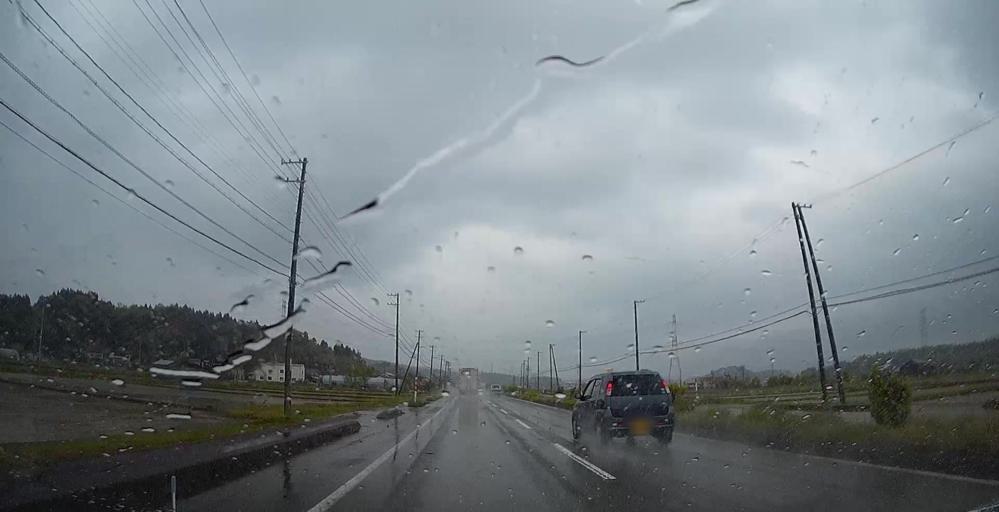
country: JP
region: Niigata
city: Kashiwazaki
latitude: 37.4367
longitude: 138.6269
